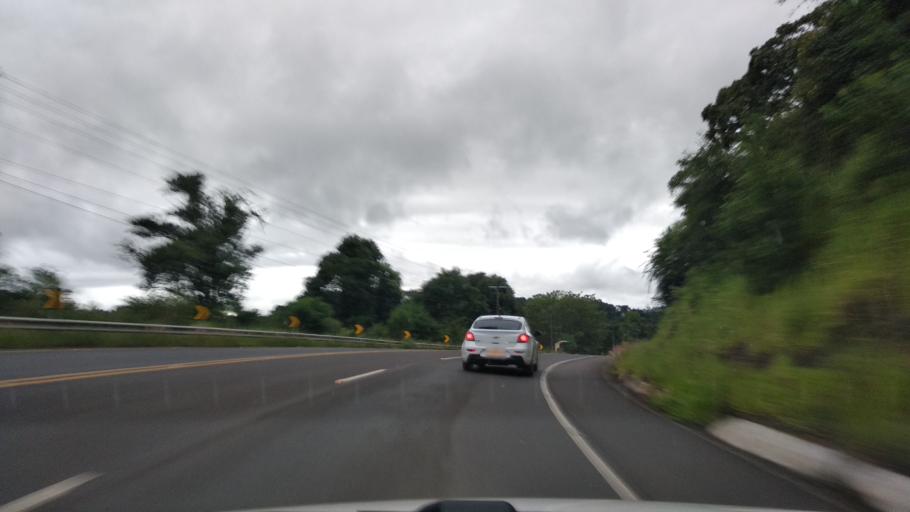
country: BR
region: Santa Catarina
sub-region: Videira
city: Videira
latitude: -27.0507
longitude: -51.2036
